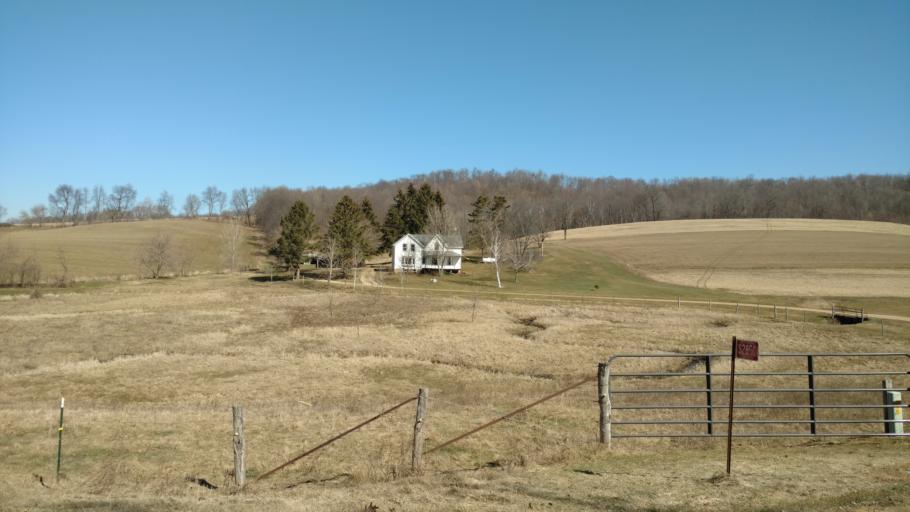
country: US
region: Wisconsin
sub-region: Vernon County
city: Hillsboro
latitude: 43.6305
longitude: -90.3441
